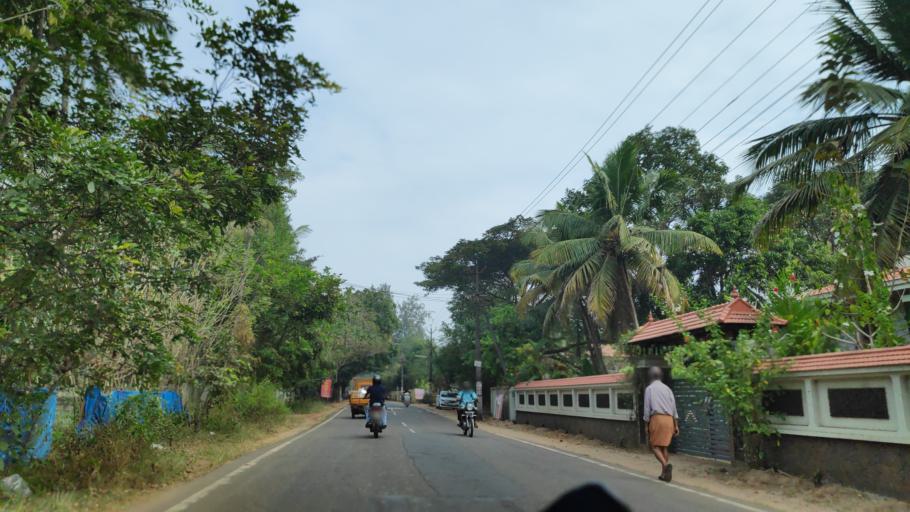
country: IN
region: Kerala
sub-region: Alappuzha
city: Vayalar
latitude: 9.7170
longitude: 76.3597
